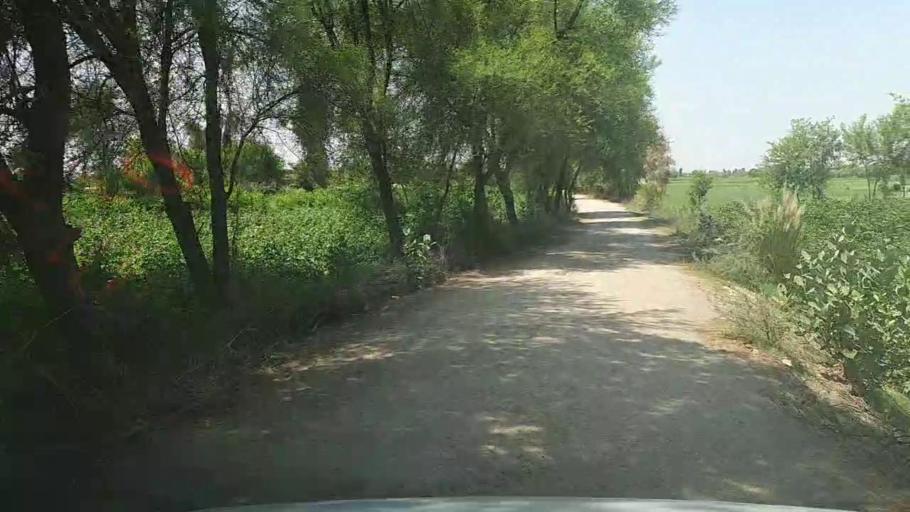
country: PK
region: Sindh
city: Ubauro
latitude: 28.1776
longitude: 69.7097
